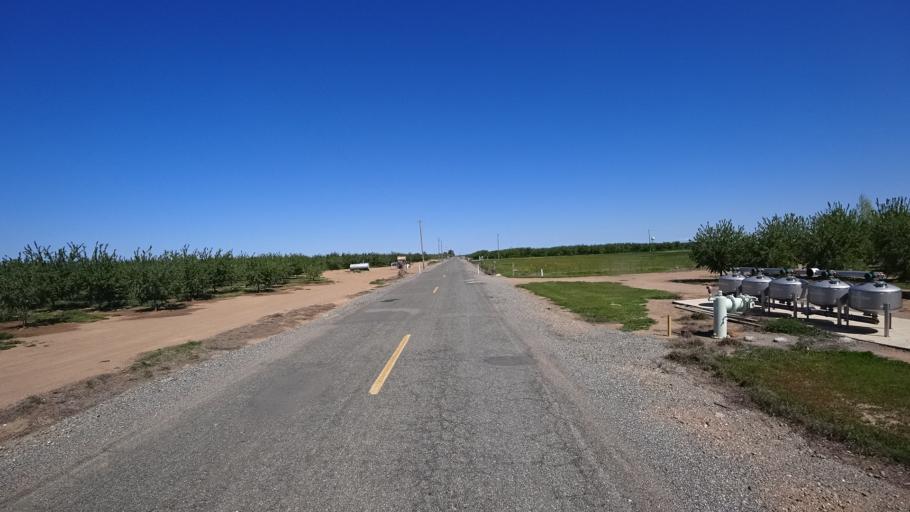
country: US
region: California
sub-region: Glenn County
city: Orland
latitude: 39.6713
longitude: -122.2531
